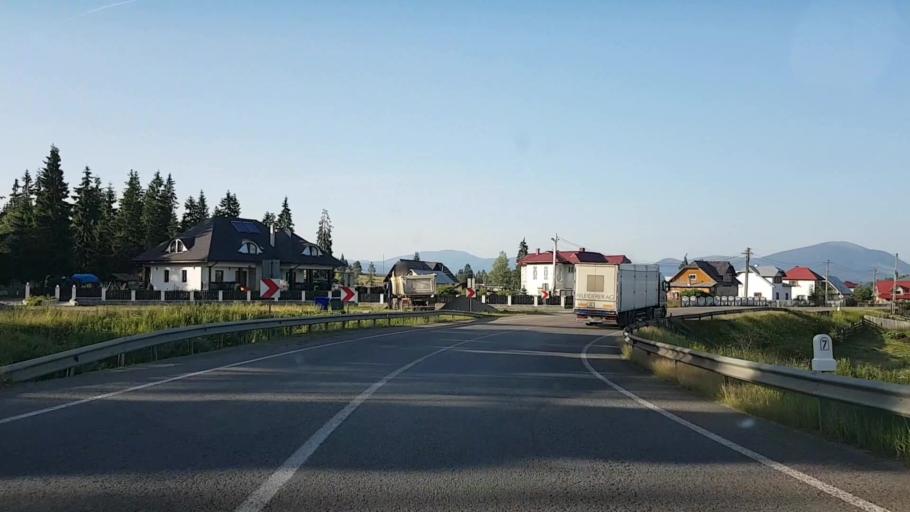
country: RO
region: Suceava
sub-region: Comuna Poiana Stampei
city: Poiana Stampei
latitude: 47.3074
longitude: 25.1227
